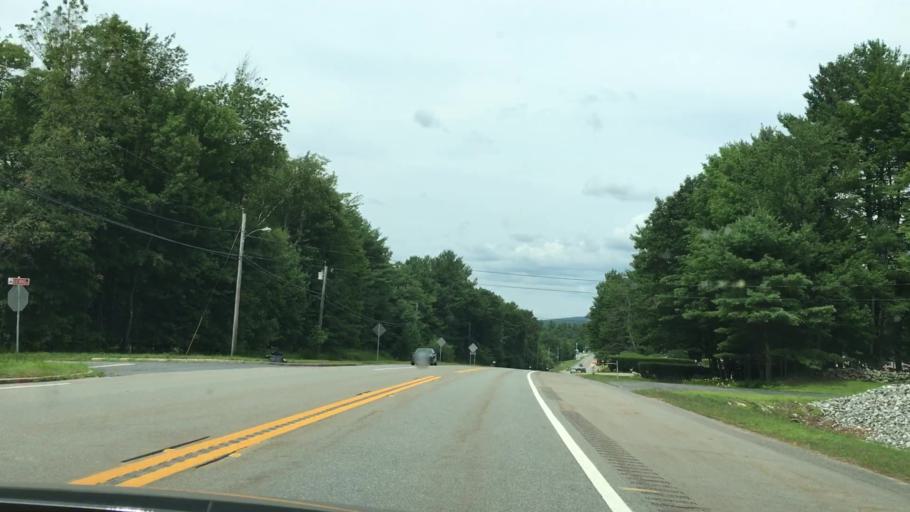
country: US
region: Massachusetts
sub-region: Worcester County
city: Gardner
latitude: 42.6342
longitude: -72.0069
